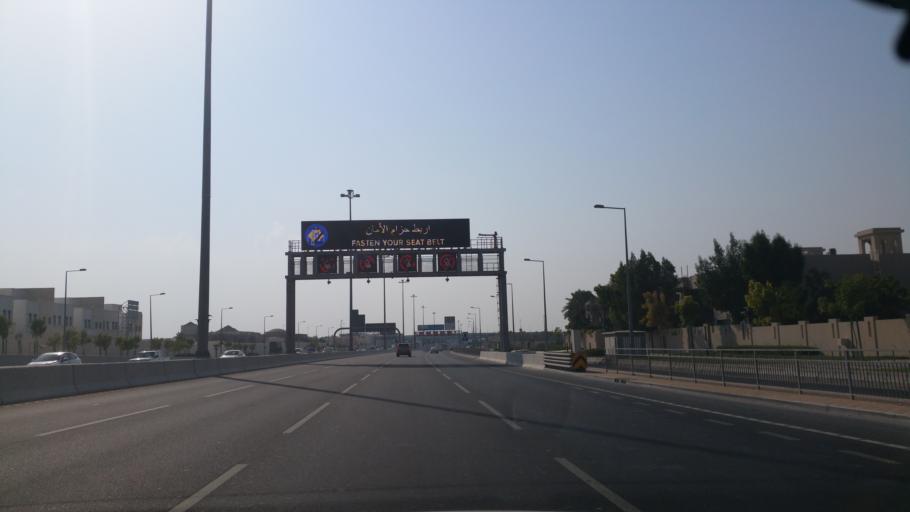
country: QA
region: Baladiyat ar Rayyan
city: Ar Rayyan
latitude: 25.2954
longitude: 51.4559
